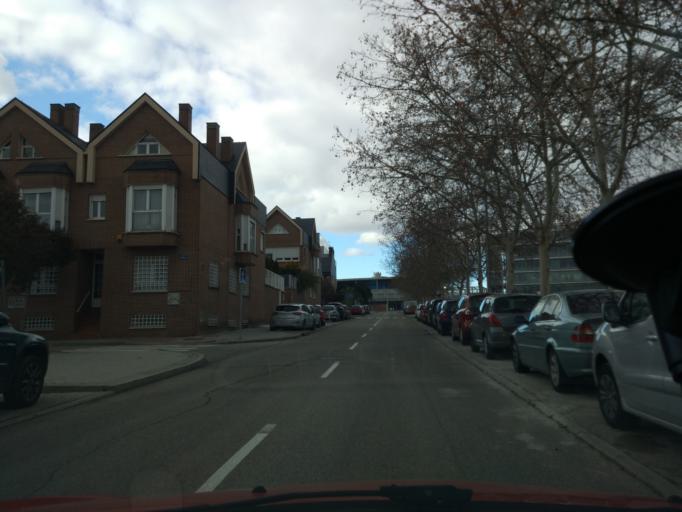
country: ES
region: Madrid
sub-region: Provincia de Madrid
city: Ciudad Lineal
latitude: 40.4460
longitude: -3.6328
